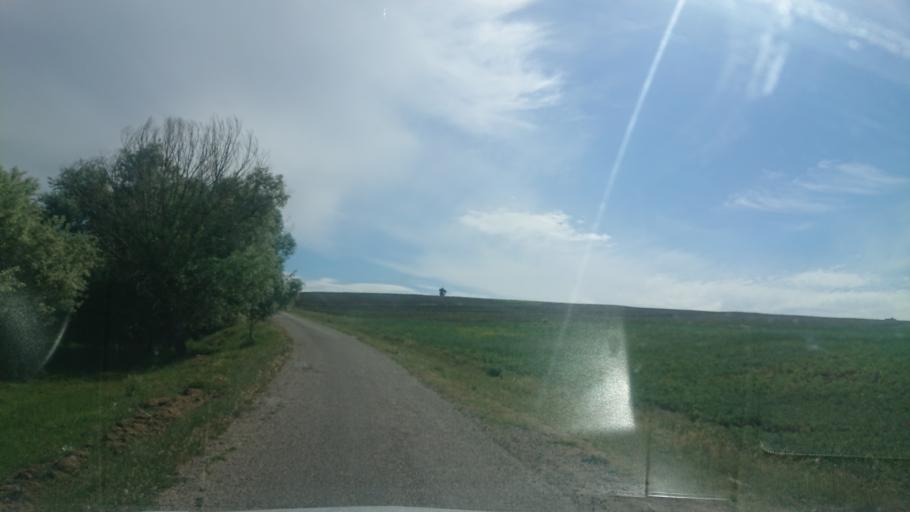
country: TR
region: Aksaray
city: Ortakoy
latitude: 38.8149
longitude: 33.9967
